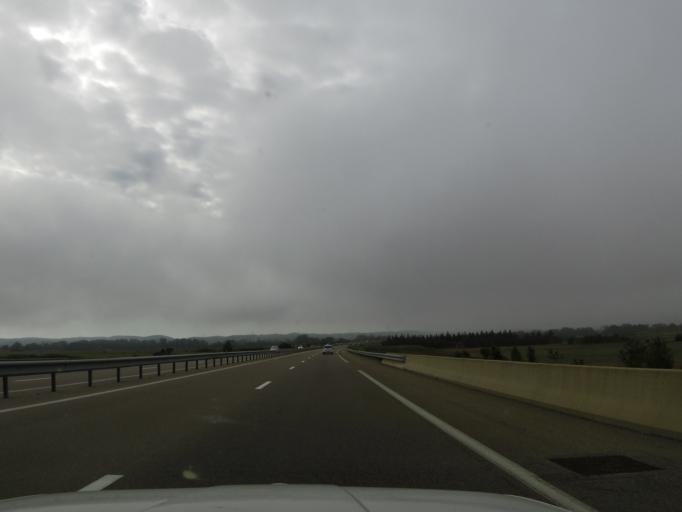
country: FR
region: Languedoc-Roussillon
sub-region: Departement du Gard
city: La Calmette
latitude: 43.9404
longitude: 4.2527
